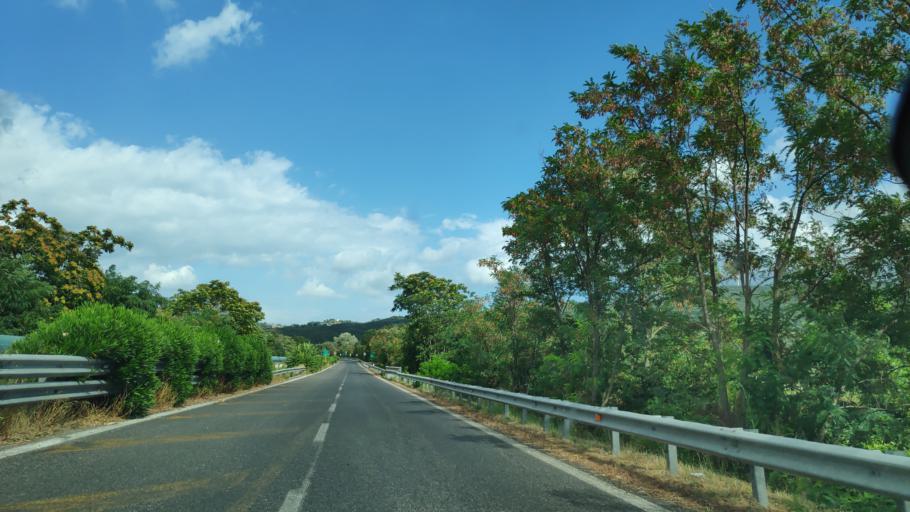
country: IT
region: Campania
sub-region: Provincia di Salerno
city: Serre
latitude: 40.6160
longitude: 15.1726
